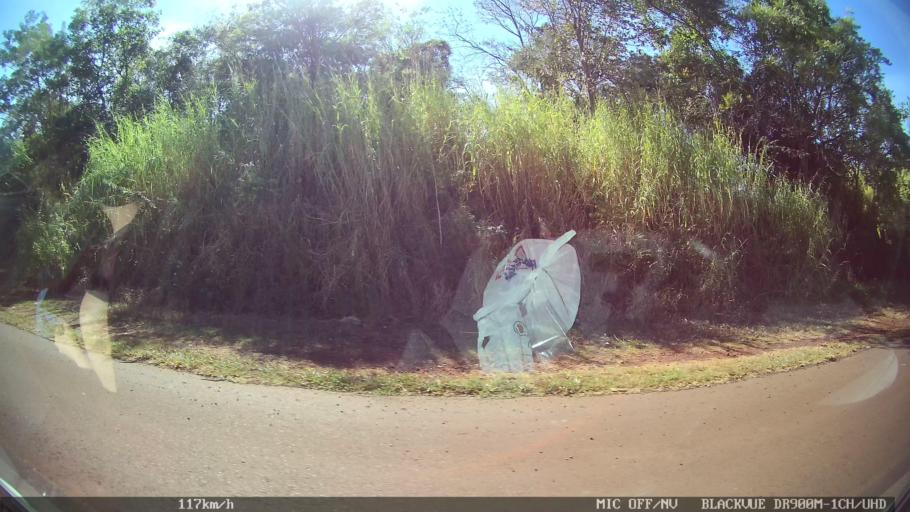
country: BR
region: Sao Paulo
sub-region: Ipua
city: Ipua
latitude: -20.4604
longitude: -48.1439
